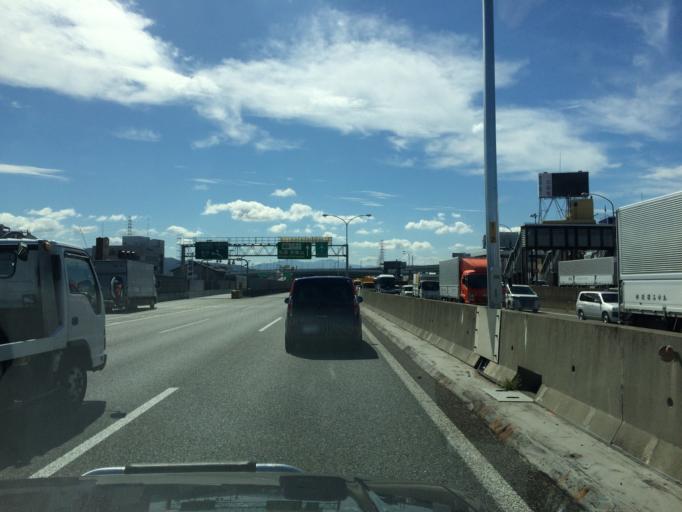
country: JP
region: Osaka
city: Daitocho
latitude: 34.6829
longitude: 135.5957
